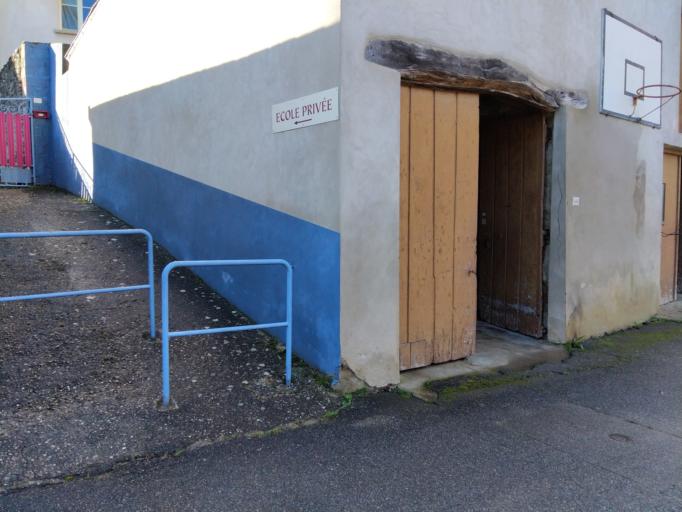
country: FR
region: Rhone-Alpes
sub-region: Departement de l'Ardeche
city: Andance
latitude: 45.2466
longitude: 4.7789
